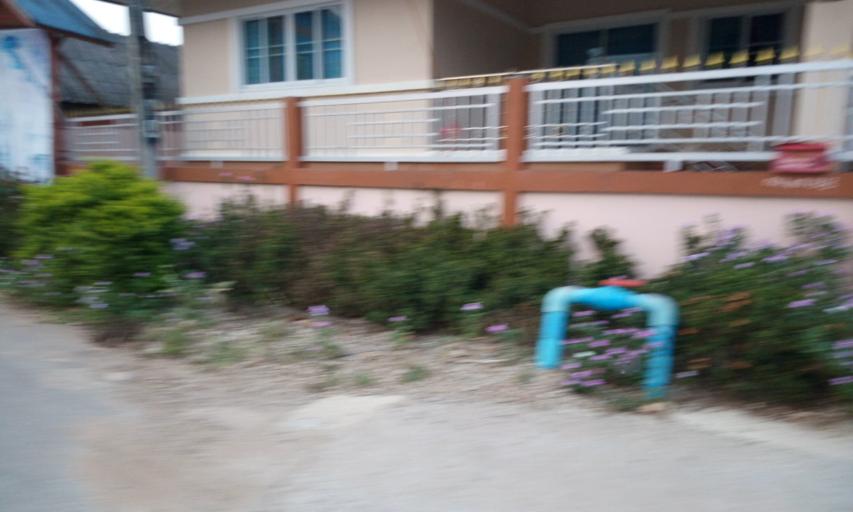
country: TH
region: Phayao
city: Phu Sang
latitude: 19.6153
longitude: 100.3254
